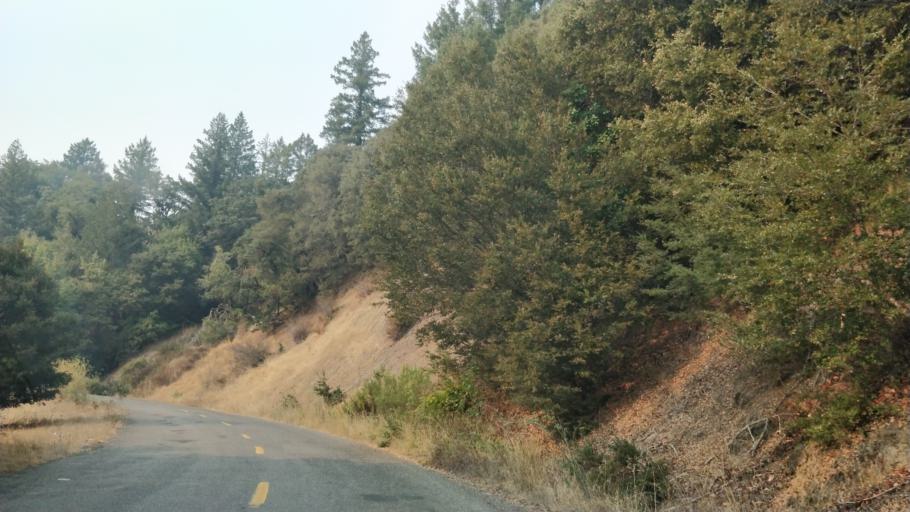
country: US
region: California
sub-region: Humboldt County
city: Rio Dell
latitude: 40.2491
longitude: -124.1218
